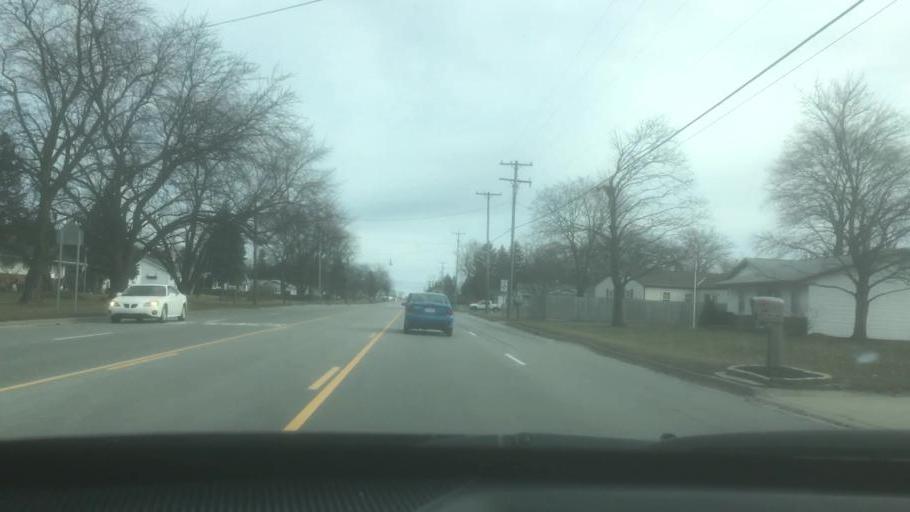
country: US
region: Michigan
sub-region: Bay County
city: Bay City
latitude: 43.6239
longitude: -83.9226
